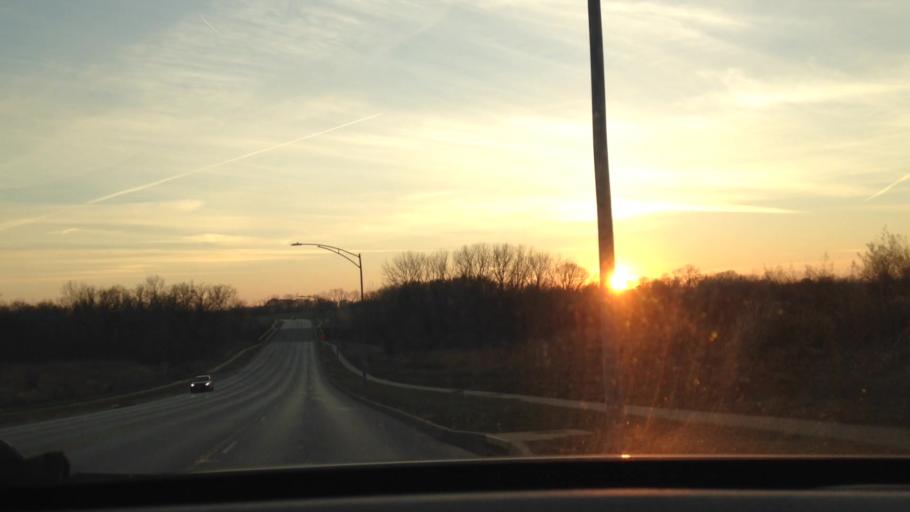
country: US
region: Missouri
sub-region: Clay County
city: Liberty
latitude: 39.2157
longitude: -94.4403
